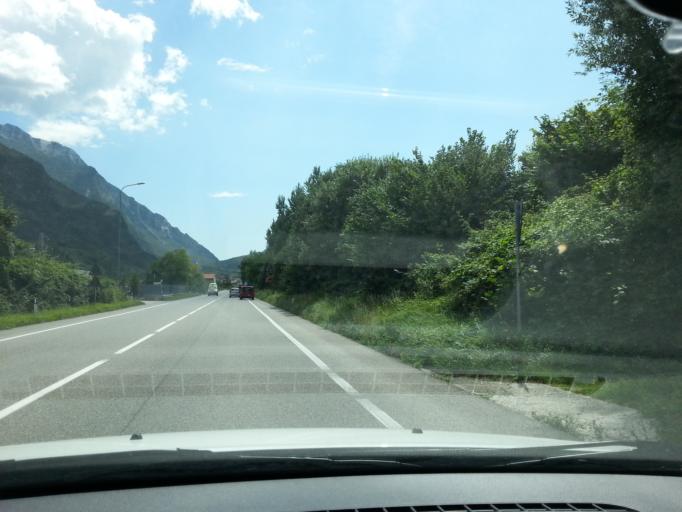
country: IT
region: Friuli Venezia Giulia
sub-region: Provincia di Udine
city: Venzone
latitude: 46.3428
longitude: 13.1396
